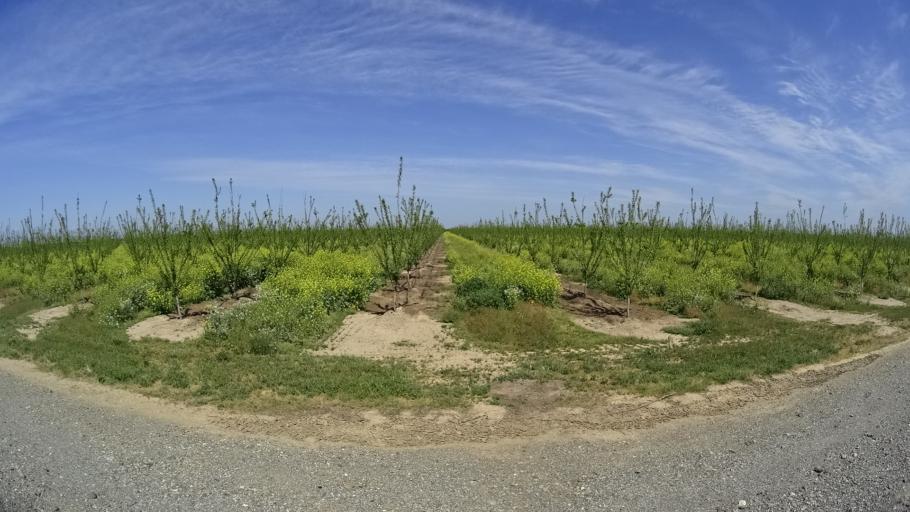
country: US
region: California
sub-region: Glenn County
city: Orland
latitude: 39.6527
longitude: -122.1393
